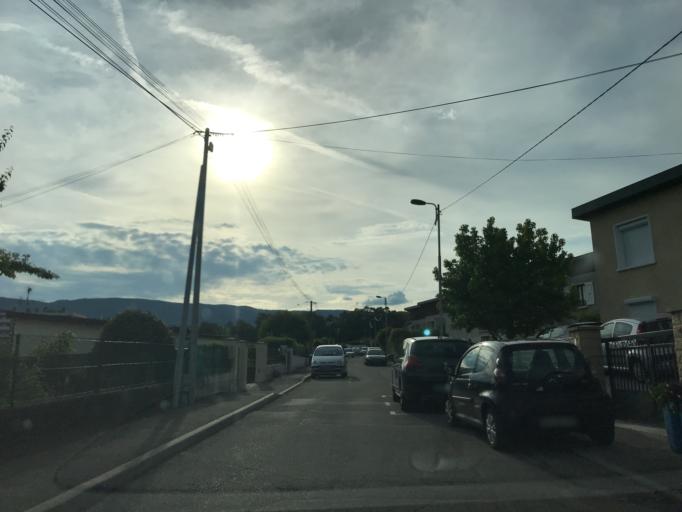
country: FR
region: Rhone-Alpes
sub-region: Departement de la Savoie
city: Cognin
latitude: 45.5645
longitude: 5.9062
